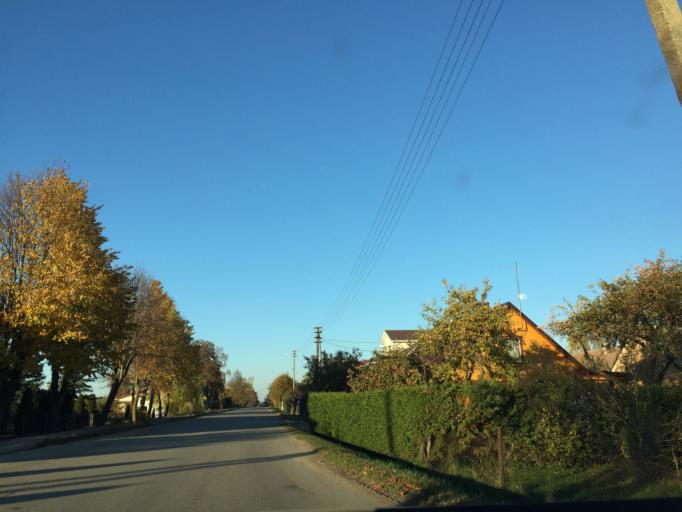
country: LT
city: Vieksniai
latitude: 56.2451
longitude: 22.5190
